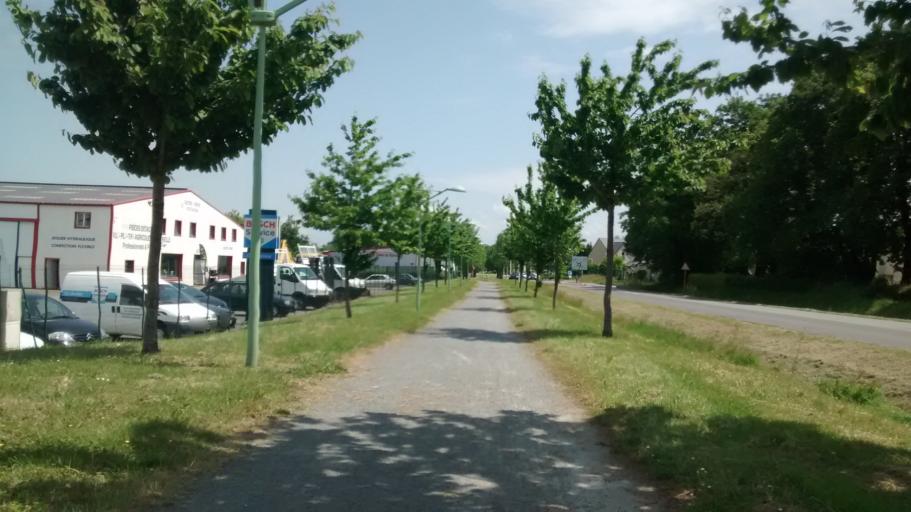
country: FR
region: Brittany
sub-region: Departement du Morbihan
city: Questembert
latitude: 47.6677
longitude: -2.4452
